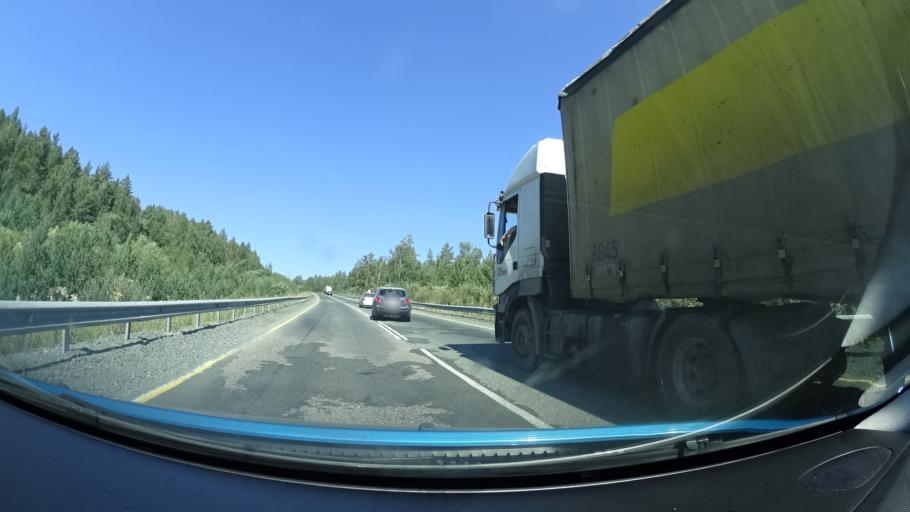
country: RU
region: Bashkortostan
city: Abzakovo
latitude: 53.8874
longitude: 58.5264
